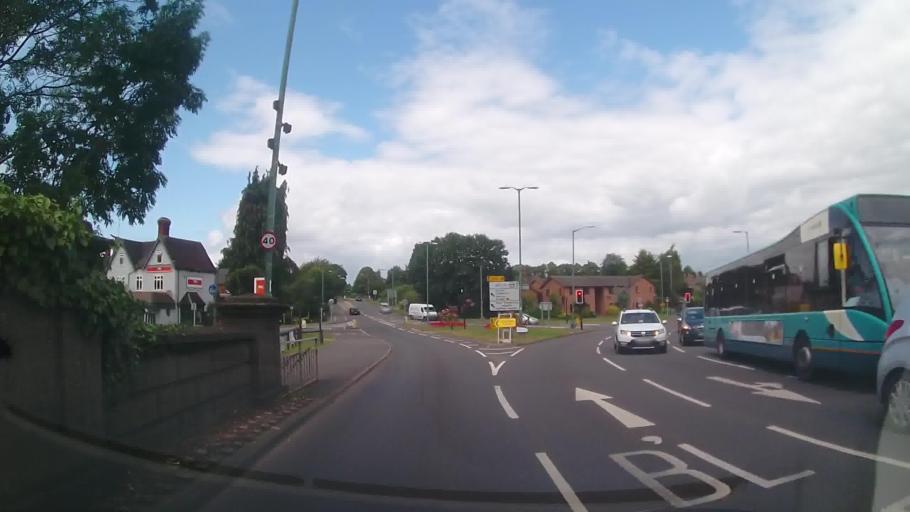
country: GB
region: England
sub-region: Shropshire
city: Bayston Hill
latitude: 52.6919
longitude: -2.7554
